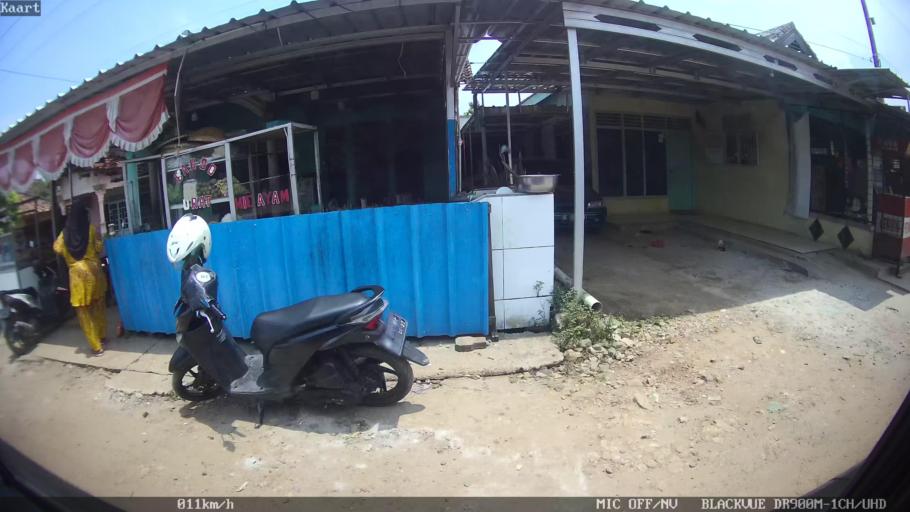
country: ID
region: Lampung
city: Natar
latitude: -5.3144
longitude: 105.2116
